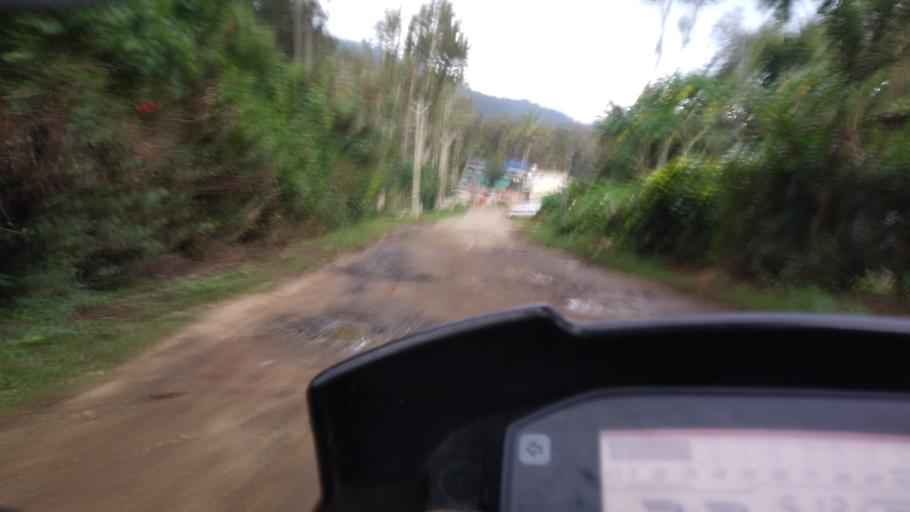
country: IN
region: Tamil Nadu
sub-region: Theni
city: Bodinayakkanur
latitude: 10.0252
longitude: 77.2443
